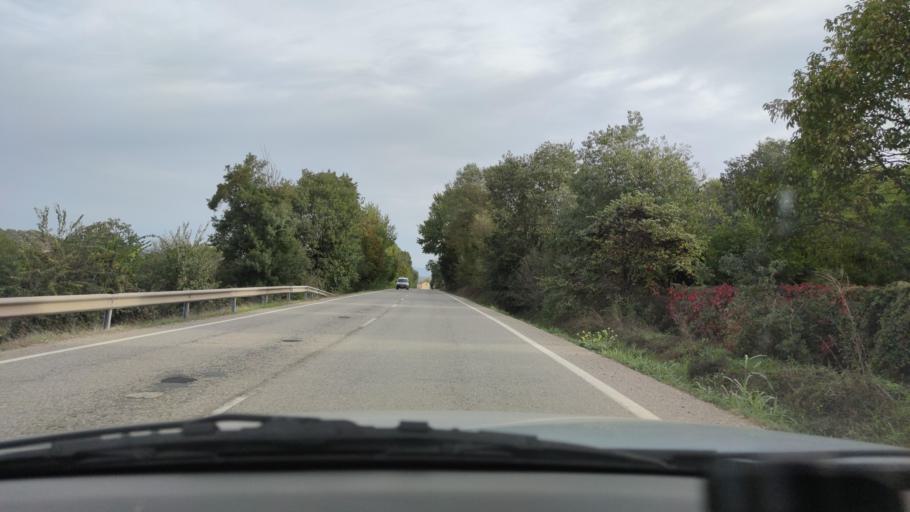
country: ES
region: Catalonia
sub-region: Provincia de Lleida
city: Artesa de Segre
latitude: 41.9028
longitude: 1.0653
